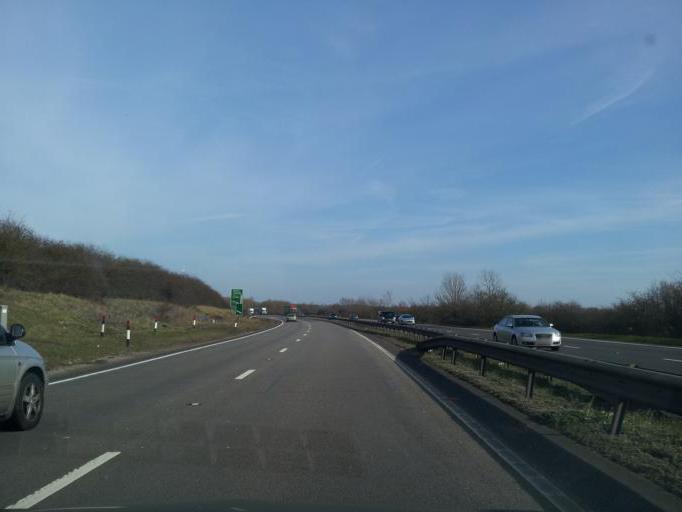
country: GB
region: England
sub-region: Northamptonshire
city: Thrapston
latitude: 52.3912
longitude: -0.5656
